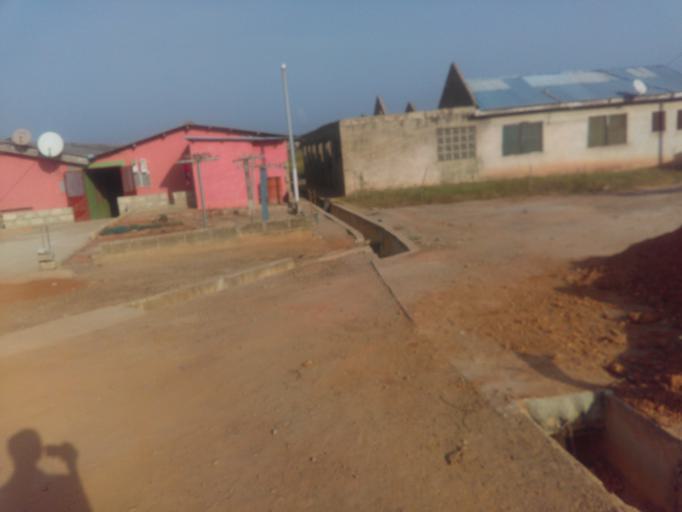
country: GH
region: Central
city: Cape Coast
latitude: 5.1085
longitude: -1.3005
